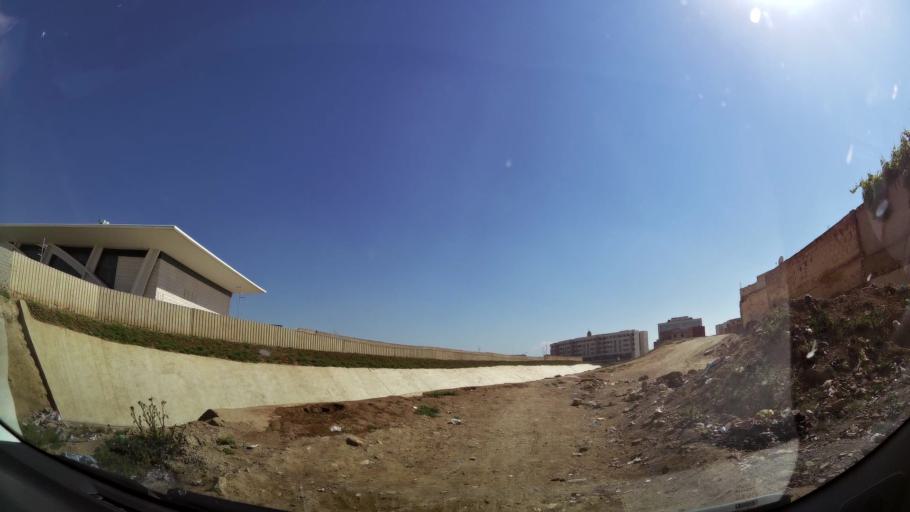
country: MA
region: Oriental
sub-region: Oujda-Angad
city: Oujda
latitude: 34.6804
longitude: -1.9258
